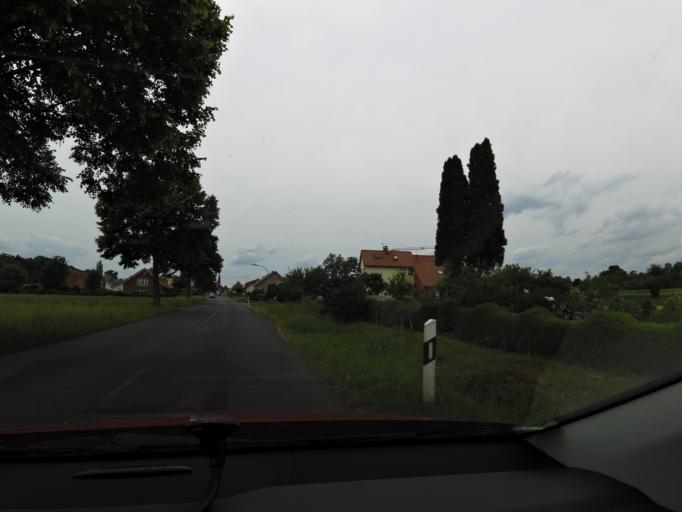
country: DE
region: Lower Saxony
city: Wollbrandshausen
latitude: 51.5881
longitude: 10.1682
